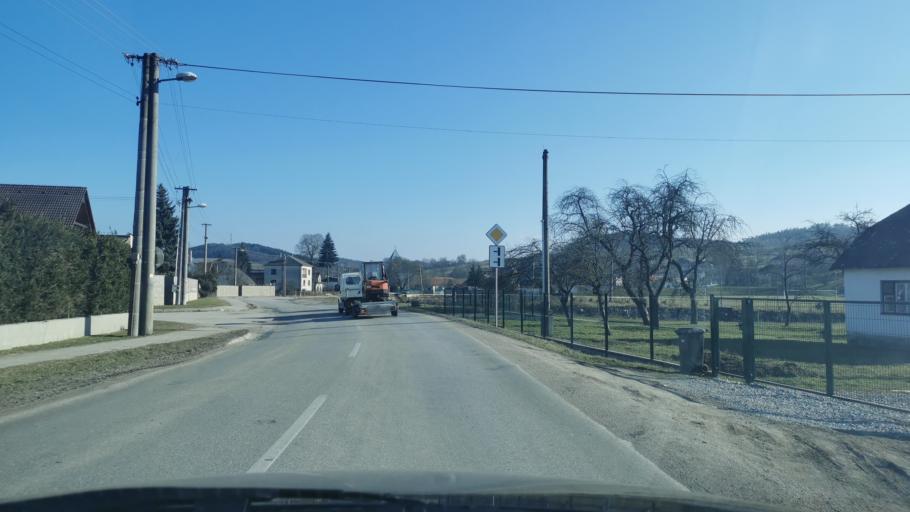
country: SK
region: Trenciansky
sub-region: Okres Myjava
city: Myjava
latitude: 48.7481
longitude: 17.5293
